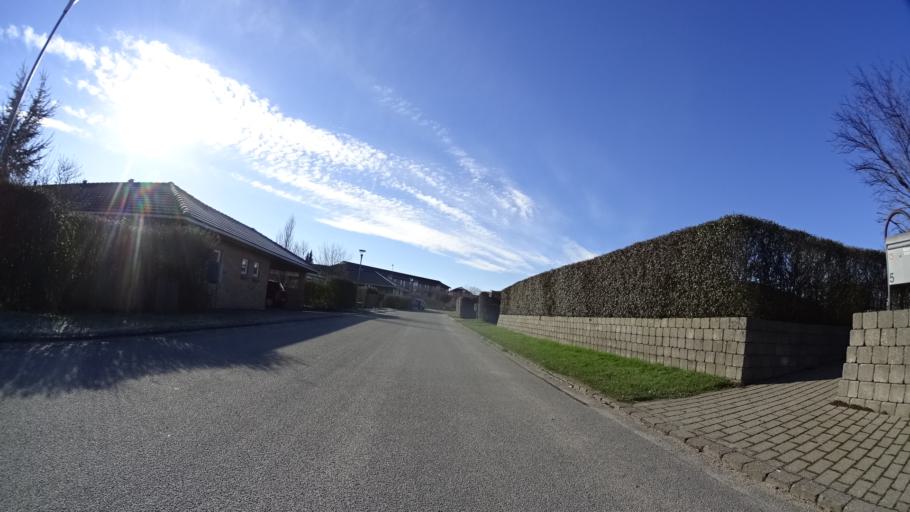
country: DK
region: Central Jutland
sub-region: Arhus Kommune
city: Kolt
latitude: 56.1123
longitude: 10.0835
